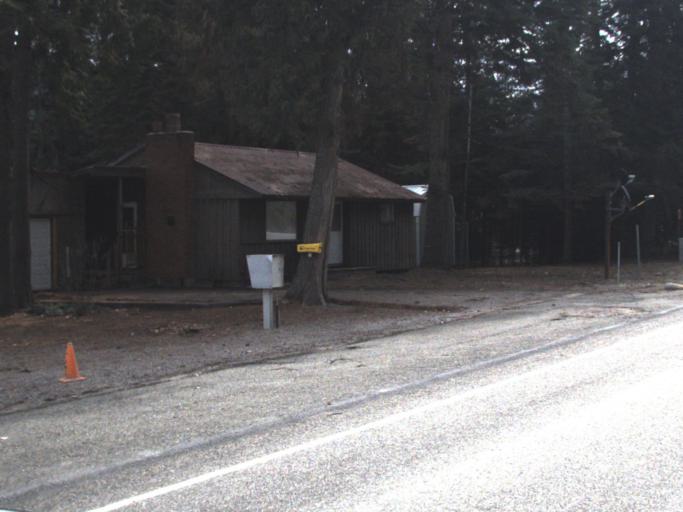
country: US
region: Washington
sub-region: Pend Oreille County
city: Newport
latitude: 48.5055
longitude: -117.2753
